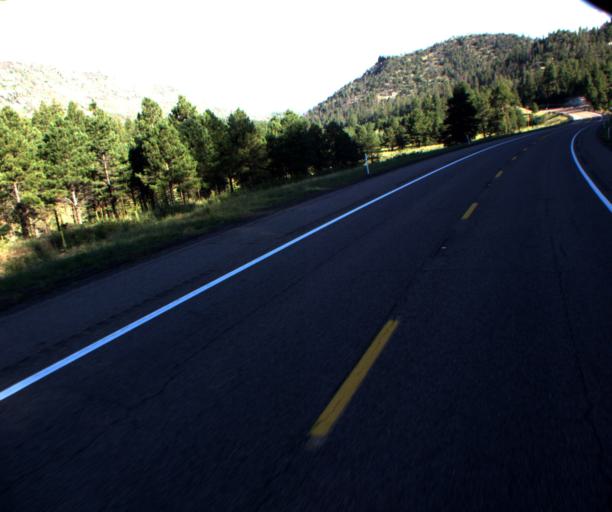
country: US
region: Arizona
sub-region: Apache County
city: Eagar
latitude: 33.9100
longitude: -109.1685
